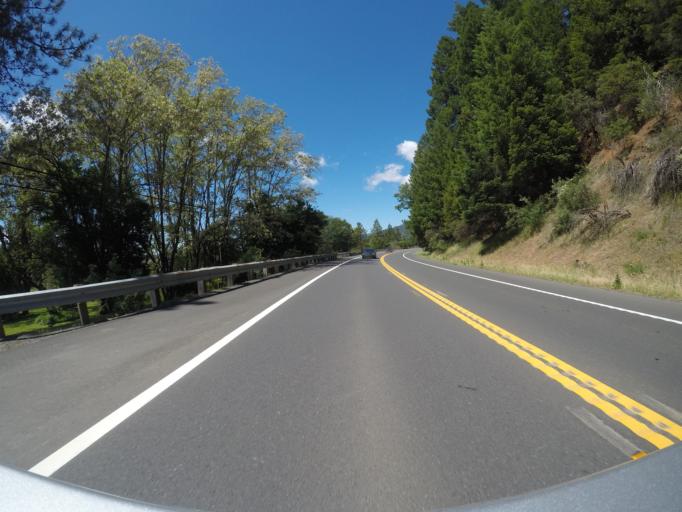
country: US
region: California
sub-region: Mendocino County
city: Laytonville
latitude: 39.6588
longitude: -123.4777
